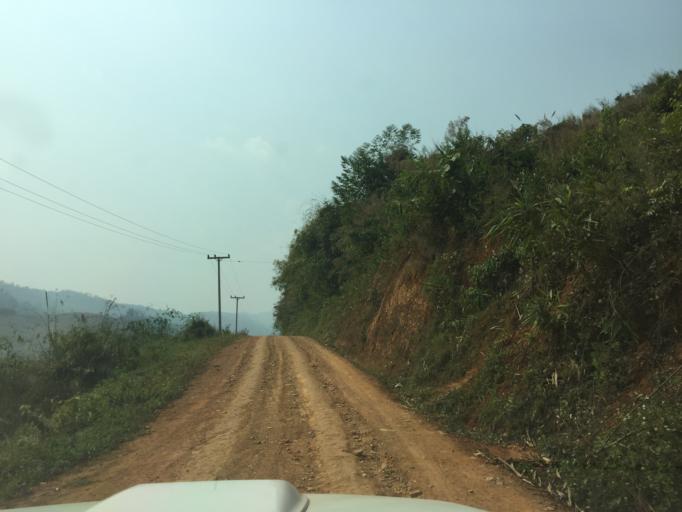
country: TH
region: Phayao
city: Phu Sang
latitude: 19.5790
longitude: 100.5275
